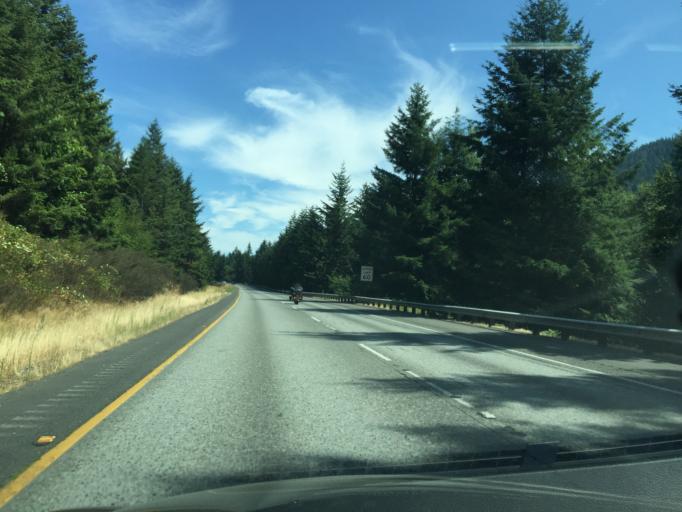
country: US
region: Washington
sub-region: Whatcom County
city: Bellingham
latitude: 48.6955
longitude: -122.4555
